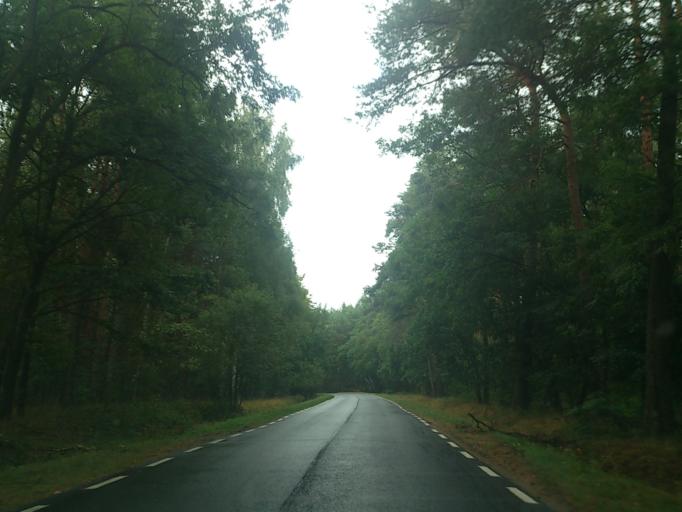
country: PL
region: Greater Poland Voivodeship
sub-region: Powiat poznanski
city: Pobiedziska
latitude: 52.5131
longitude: 17.1995
